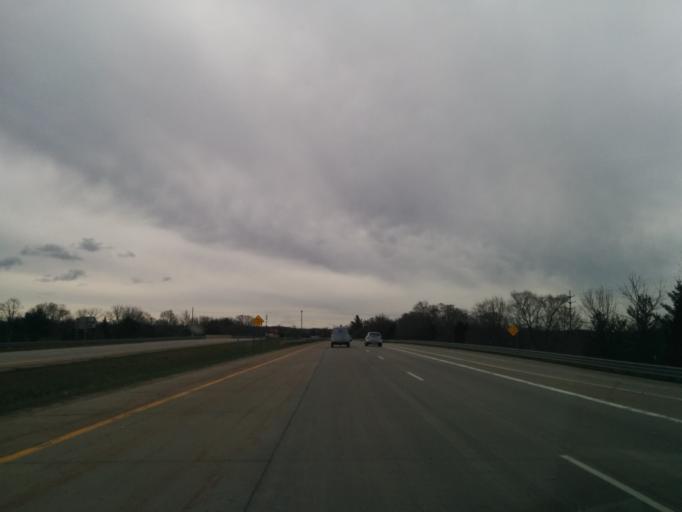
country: US
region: Michigan
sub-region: Ottawa County
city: Jenison
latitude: 42.9018
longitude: -85.7811
